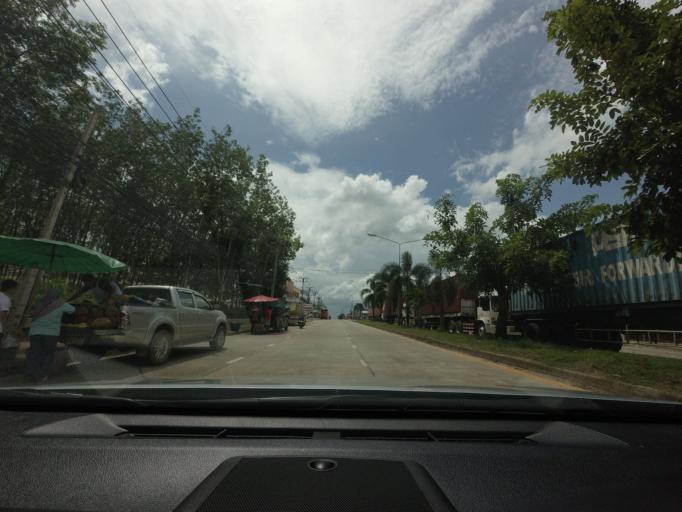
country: TH
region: Songkhla
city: Sadao
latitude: 6.5277
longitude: 100.4179
